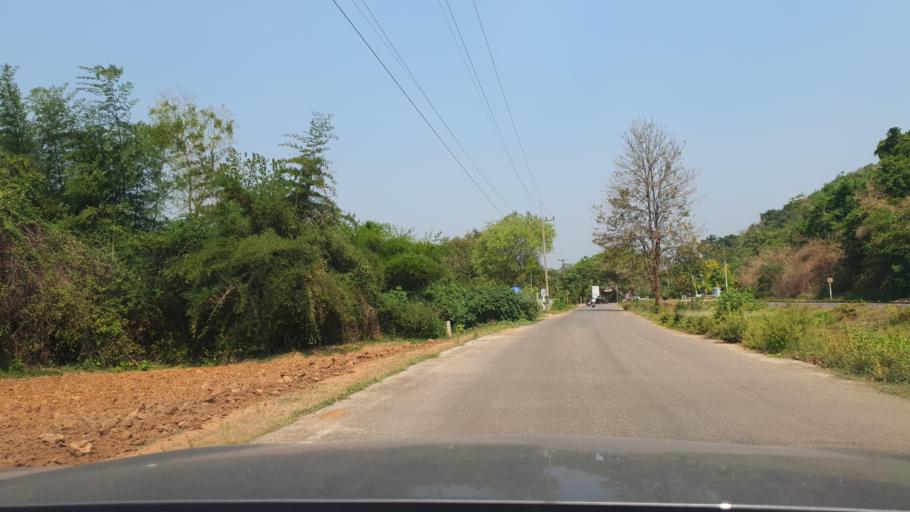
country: TH
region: Kanchanaburi
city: Sai Yok
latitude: 14.0951
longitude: 99.1763
